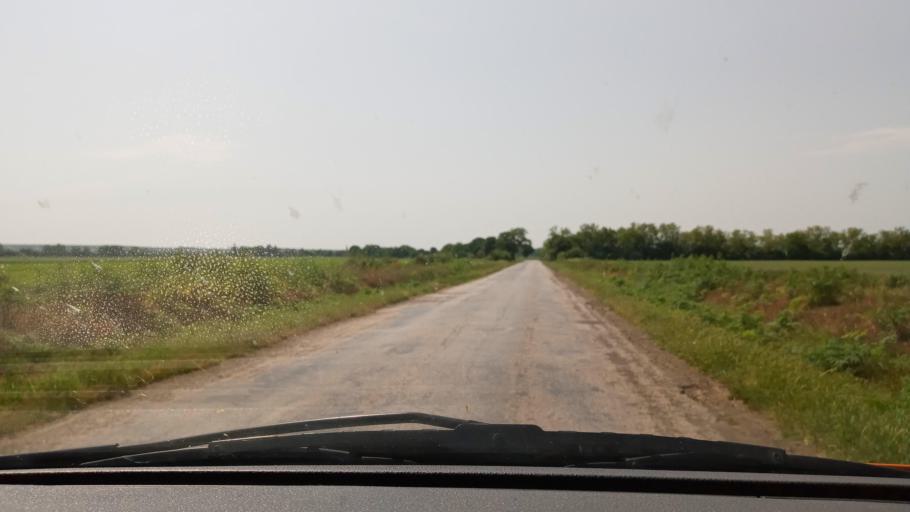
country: HU
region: Baranya
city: Szentlorinc
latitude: 46.0219
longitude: 18.0324
